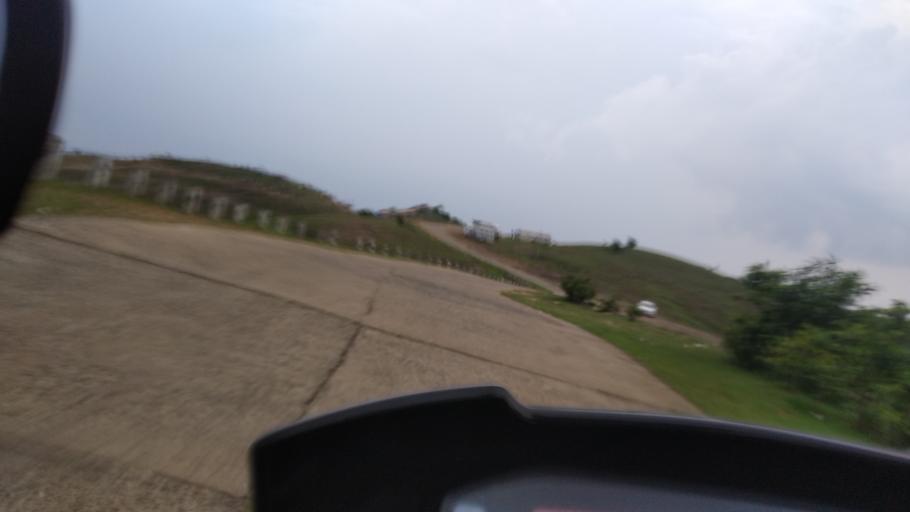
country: IN
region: Tamil Nadu
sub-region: Theni
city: Gudalur
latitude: 9.5491
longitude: 77.0332
